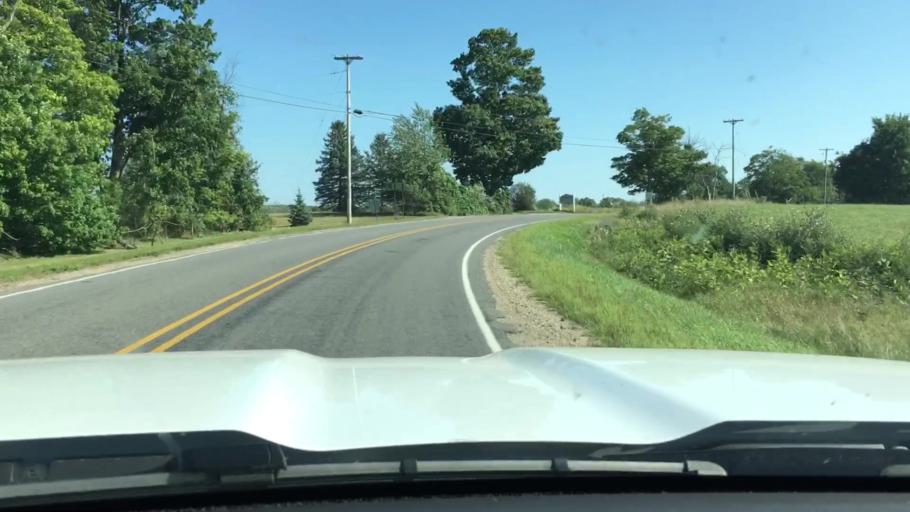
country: US
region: Michigan
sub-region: Muskegon County
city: Ravenna
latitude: 43.1821
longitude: -85.9282
